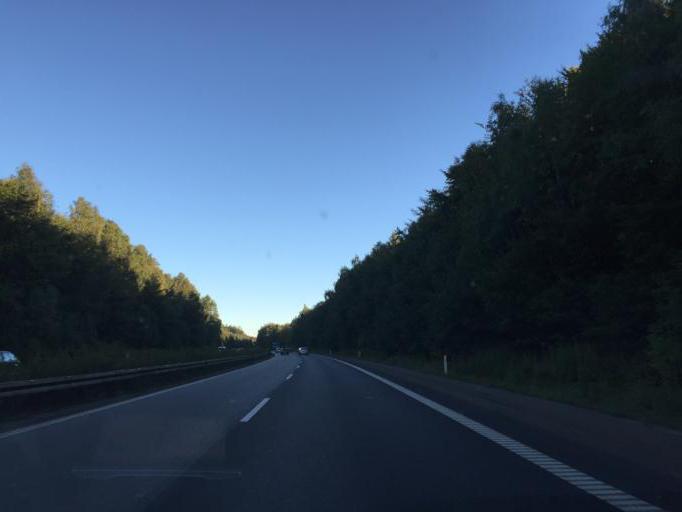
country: DK
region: Capital Region
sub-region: Fureso Kommune
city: Vaerlose
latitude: 55.7939
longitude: 12.3815
